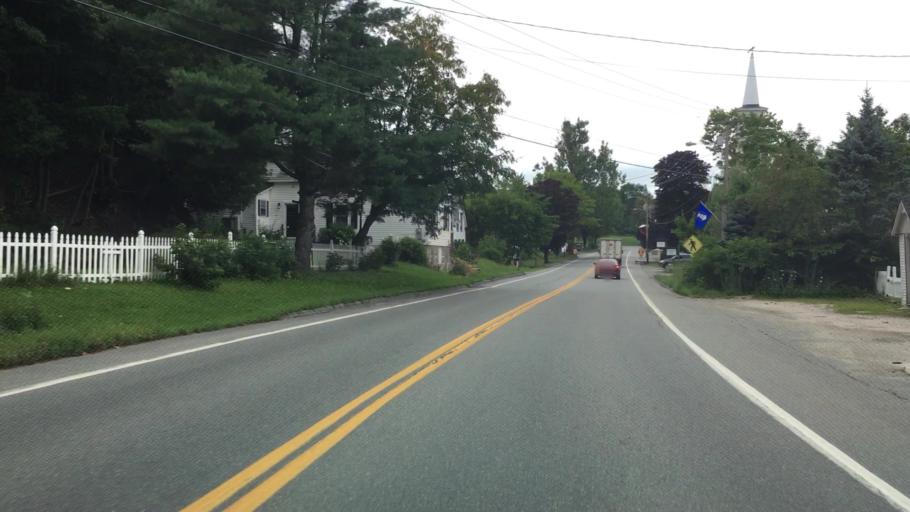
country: US
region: Maine
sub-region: Waldo County
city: Frankfort
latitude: 44.6066
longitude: -68.8734
